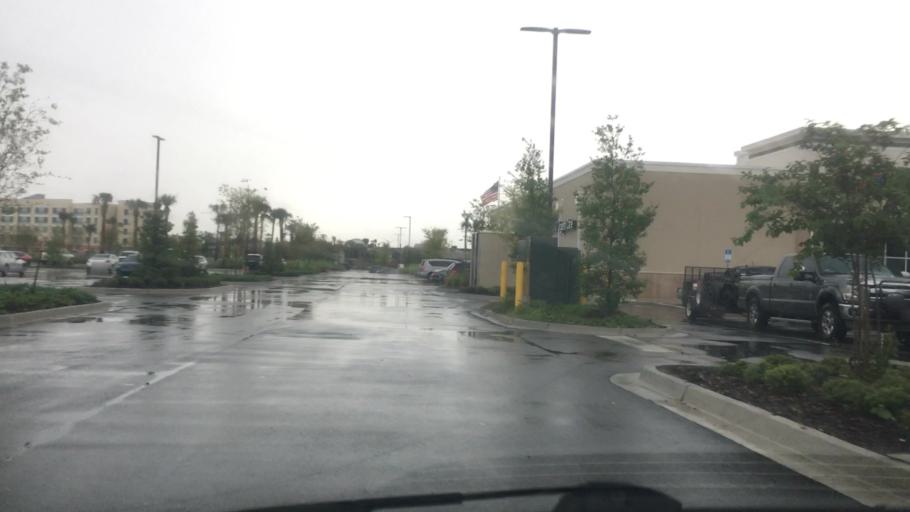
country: US
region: Florida
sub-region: Duval County
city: Jacksonville
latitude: 30.2557
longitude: -81.5337
